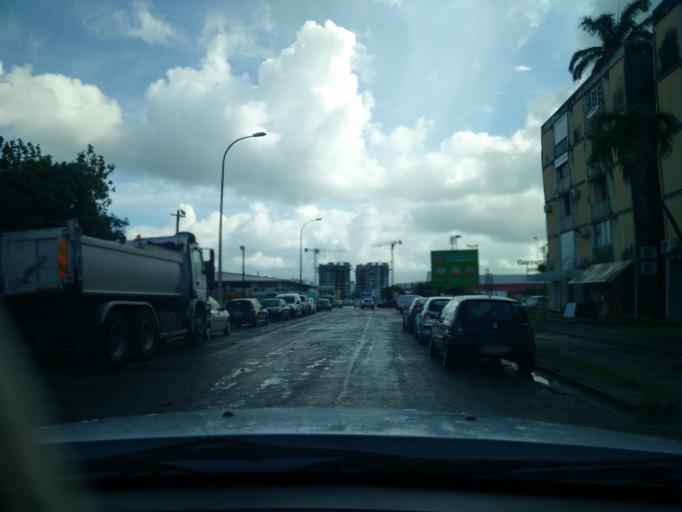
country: GP
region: Guadeloupe
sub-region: Guadeloupe
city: Pointe-a-Pitre
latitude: 16.2529
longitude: -61.5400
